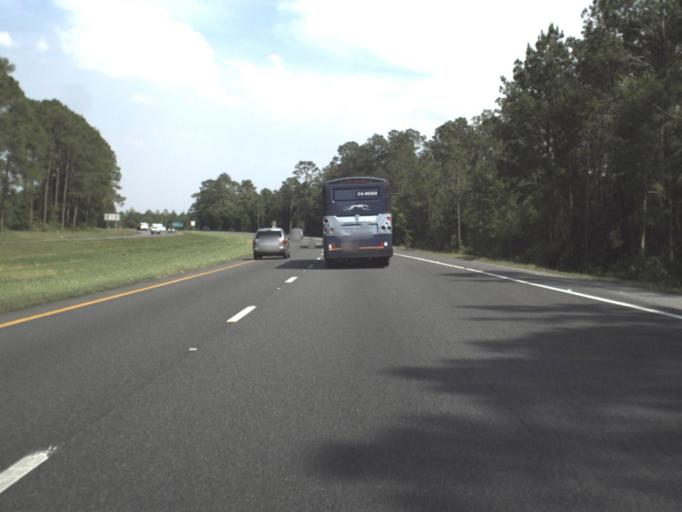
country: US
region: Florida
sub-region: Baker County
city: Macclenny
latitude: 30.2348
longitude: -82.2970
